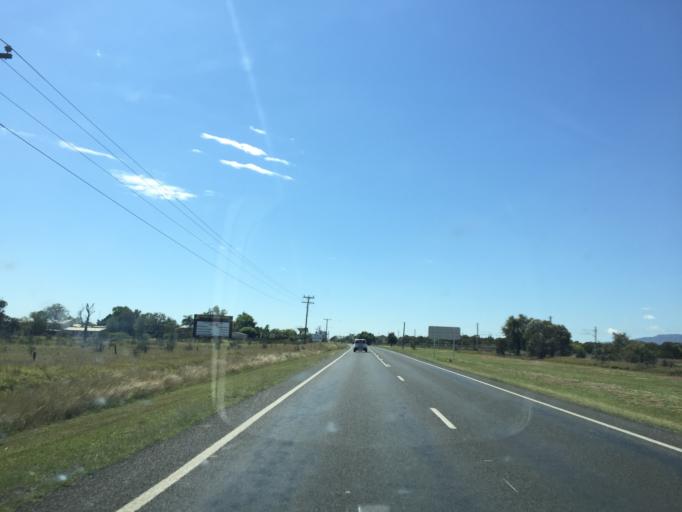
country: AU
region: Queensland
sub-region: Central Highlands
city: Blackwater
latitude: -23.5856
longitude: 148.8673
